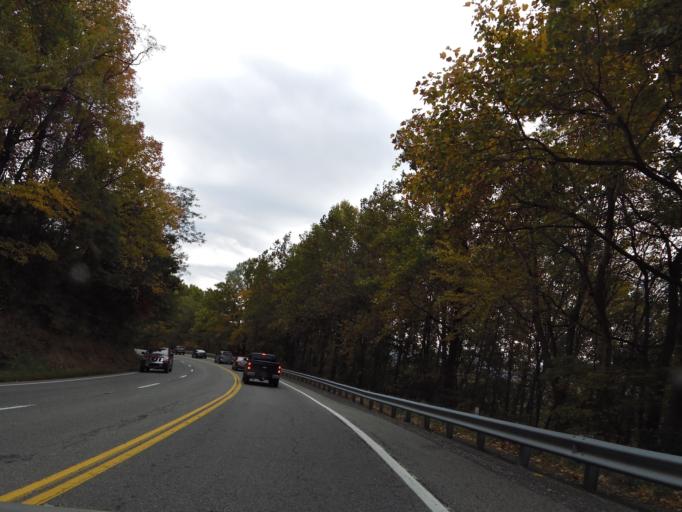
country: US
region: Virginia
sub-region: Carroll County
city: Cana
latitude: 36.6320
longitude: -80.6925
